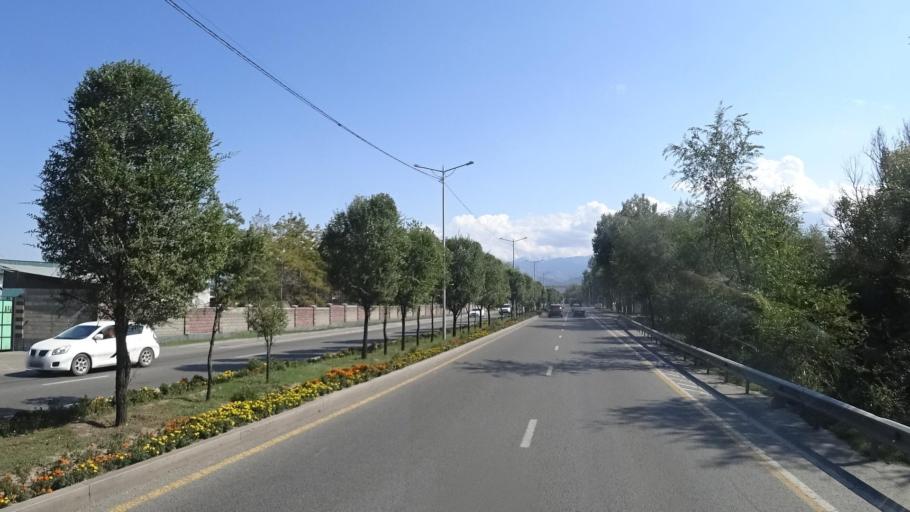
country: KZ
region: Almaty Oblysy
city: Pervomayskiy
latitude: 43.3357
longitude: 77.0027
